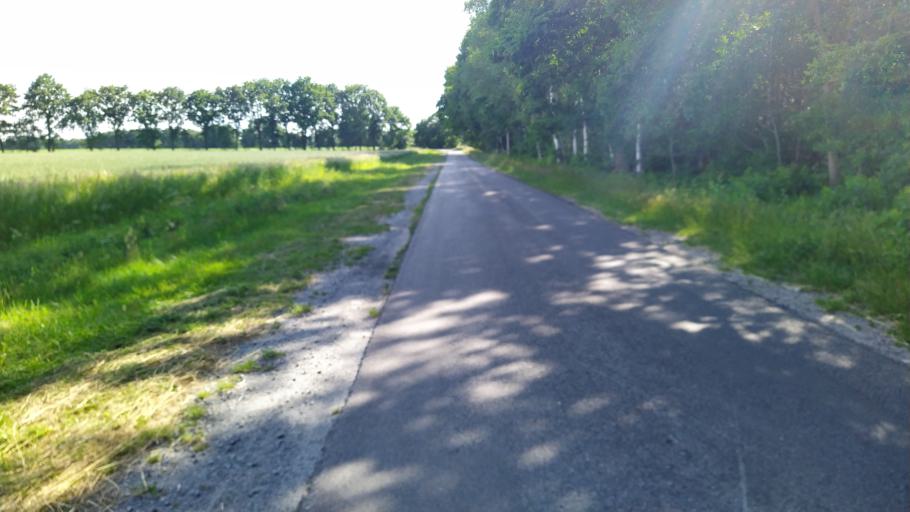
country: DE
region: Lower Saxony
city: Lintig
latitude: 53.6374
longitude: 8.8990
